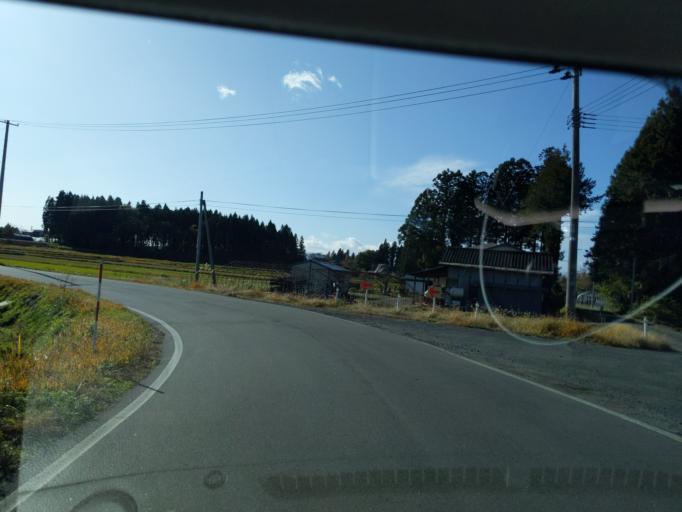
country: JP
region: Iwate
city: Mizusawa
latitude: 39.0880
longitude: 141.1113
